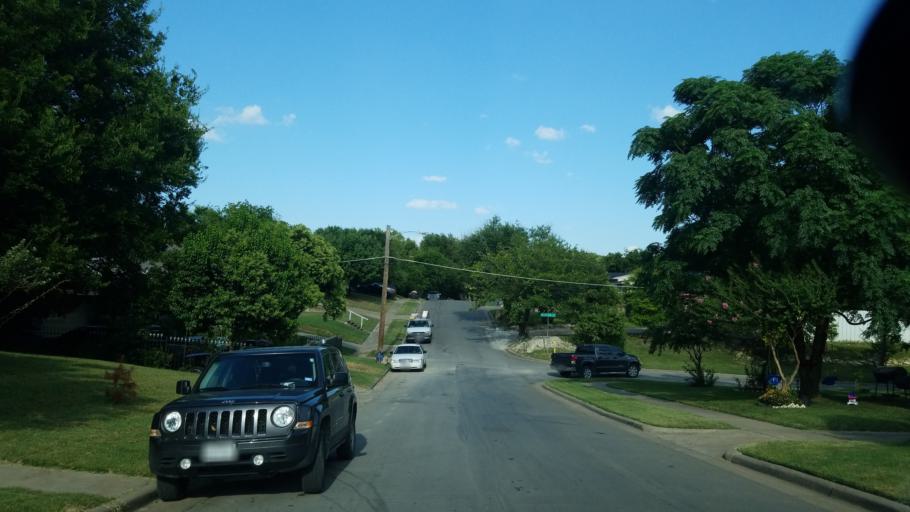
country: US
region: Texas
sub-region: Dallas County
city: Balch Springs
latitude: 32.7664
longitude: -96.7061
